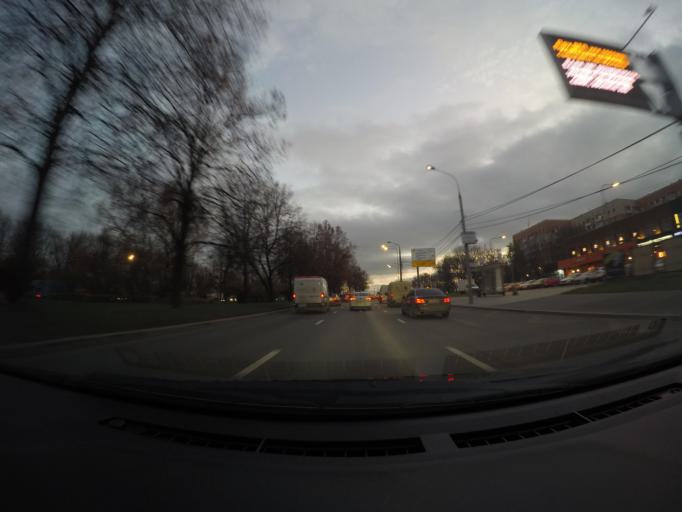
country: RU
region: Moscow
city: Kolomenskoye
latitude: 55.6695
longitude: 37.6614
